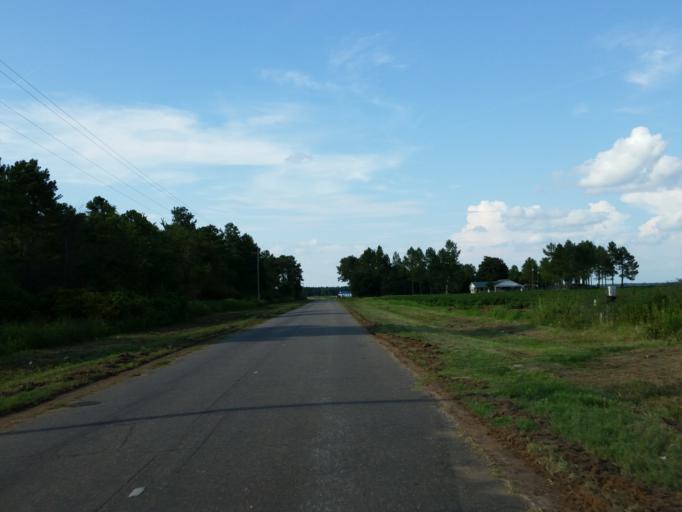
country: US
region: Georgia
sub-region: Crisp County
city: Cordele
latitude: 31.9218
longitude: -84.0095
